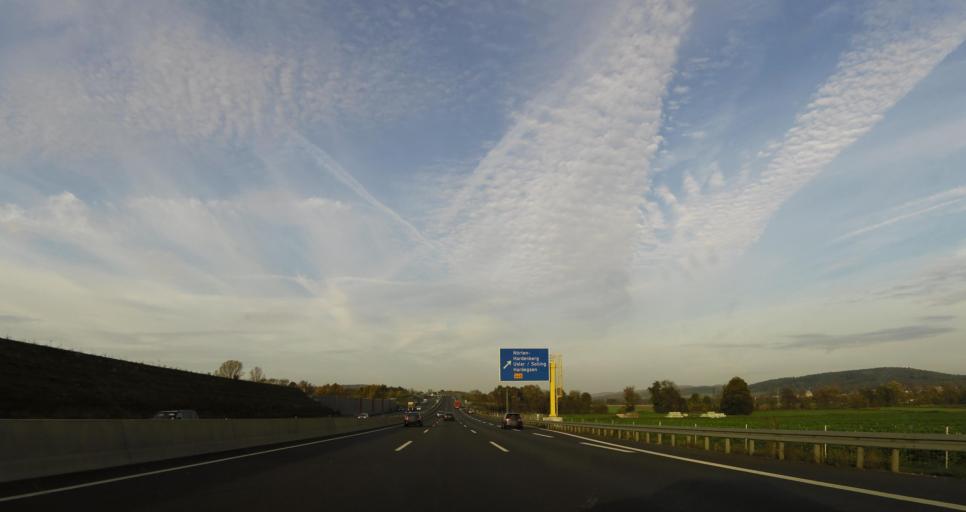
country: DE
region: Lower Saxony
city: Norten-Hardenberg
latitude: 51.6247
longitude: 9.9154
